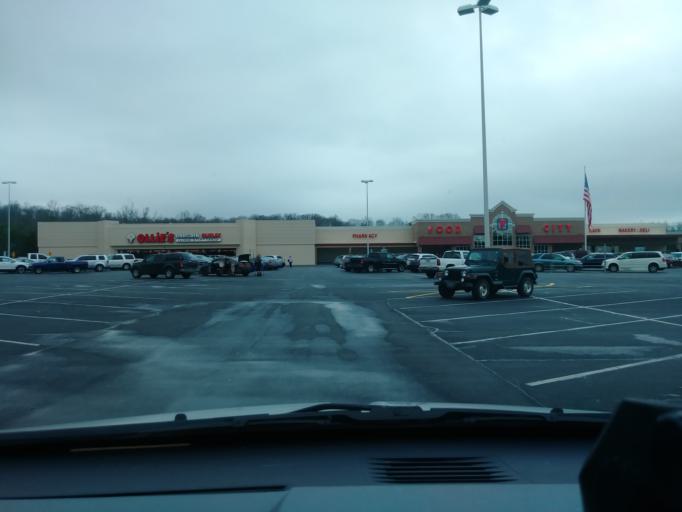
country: US
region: Tennessee
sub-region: Greene County
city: Tusculum
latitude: 36.1817
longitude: -82.7763
